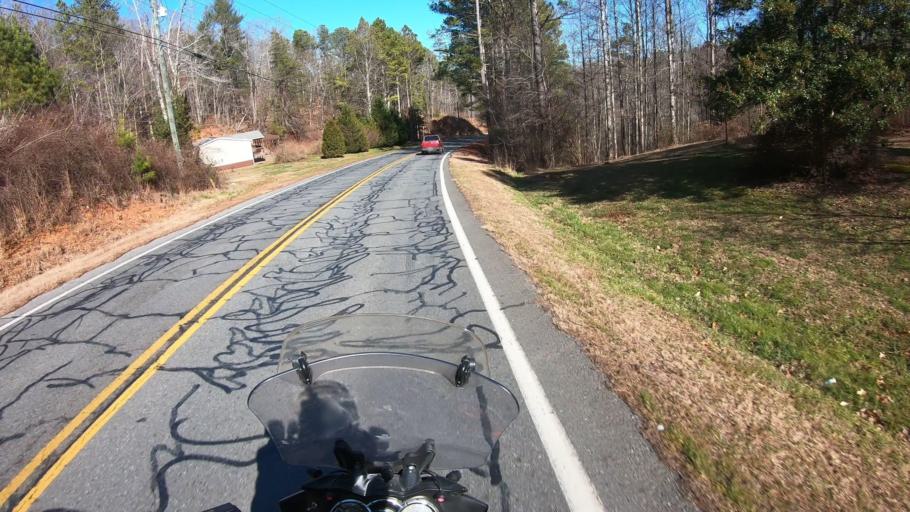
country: US
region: Georgia
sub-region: Gilmer County
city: Ellijay
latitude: 34.6375
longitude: -84.5753
